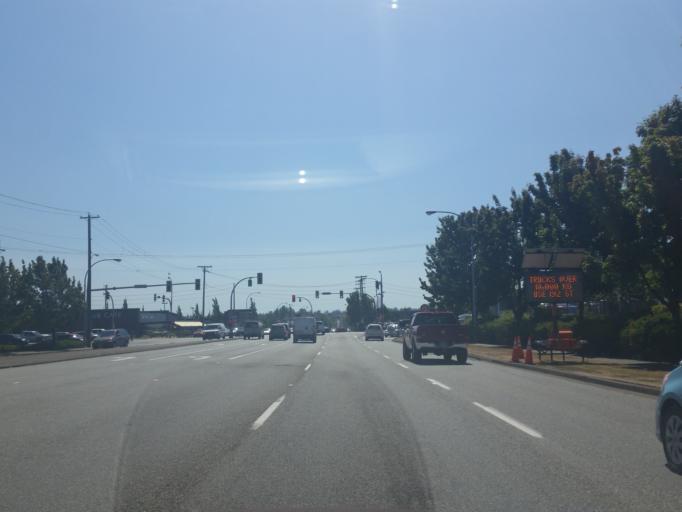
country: CA
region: British Columbia
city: Langley
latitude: 49.1145
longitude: -122.6688
